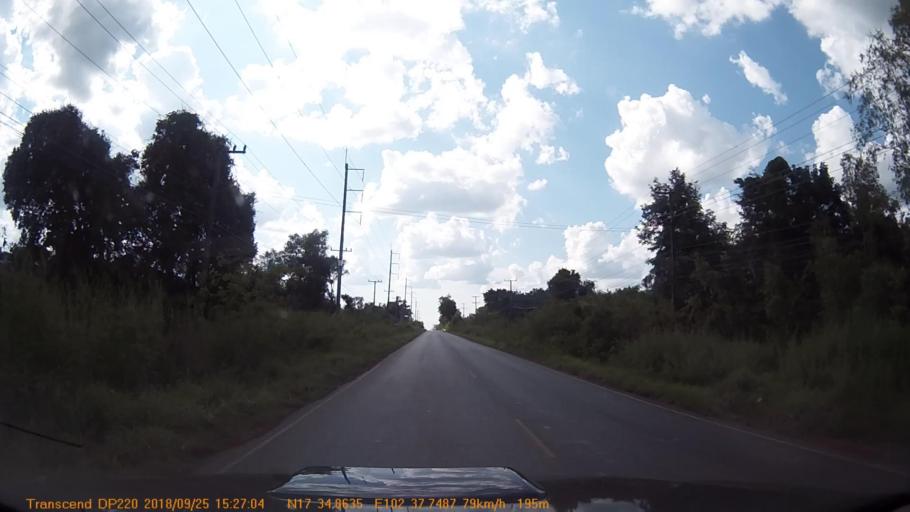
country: TH
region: Nong Khai
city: Sa Khrai
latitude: 17.5813
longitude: 102.6286
